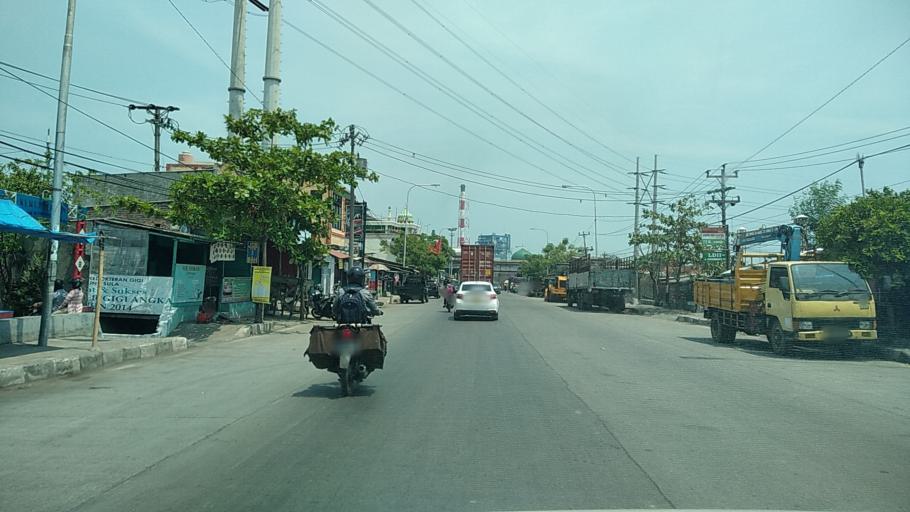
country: ID
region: Central Java
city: Semarang
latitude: -6.9564
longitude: 110.4307
